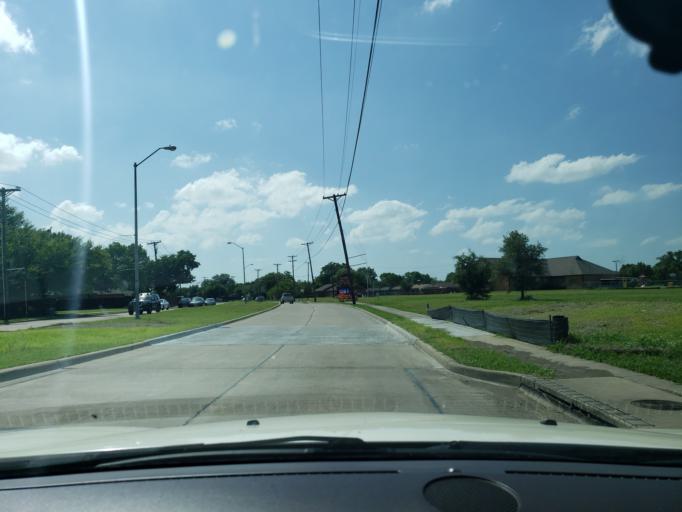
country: US
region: Texas
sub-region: Dallas County
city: Rowlett
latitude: 32.8933
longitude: -96.5598
